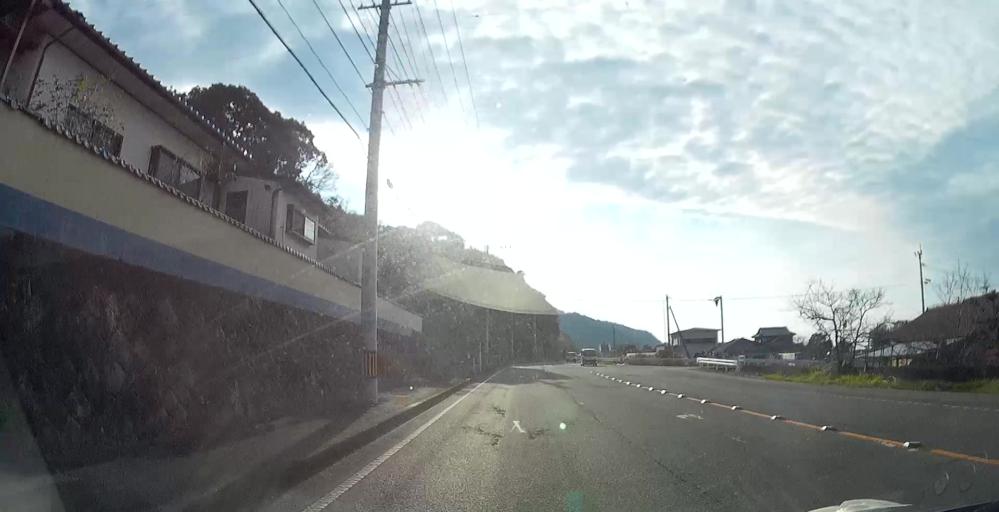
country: JP
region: Kumamoto
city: Matsubase
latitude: 32.6589
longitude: 130.5173
